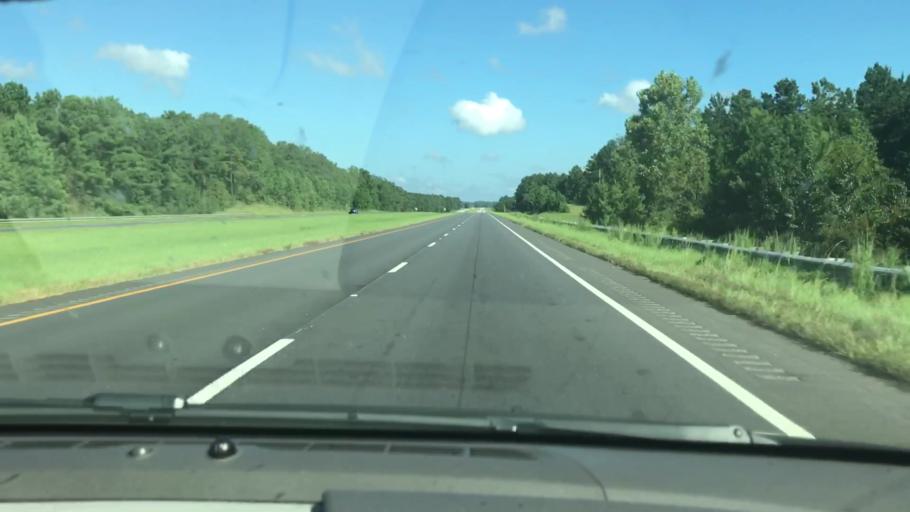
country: US
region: Alabama
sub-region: Barbour County
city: Eufaula
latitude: 32.0542
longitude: -85.1354
